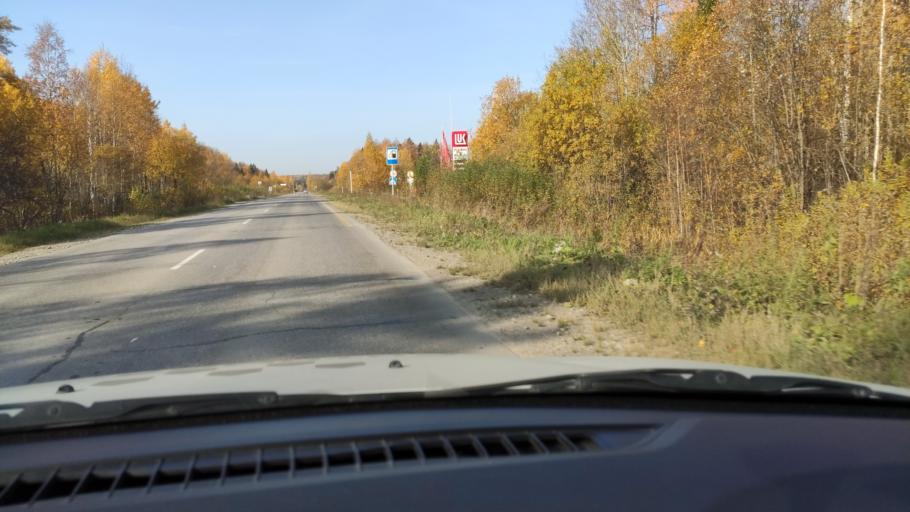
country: RU
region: Perm
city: Novyye Lyady
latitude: 58.0327
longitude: 56.6126
